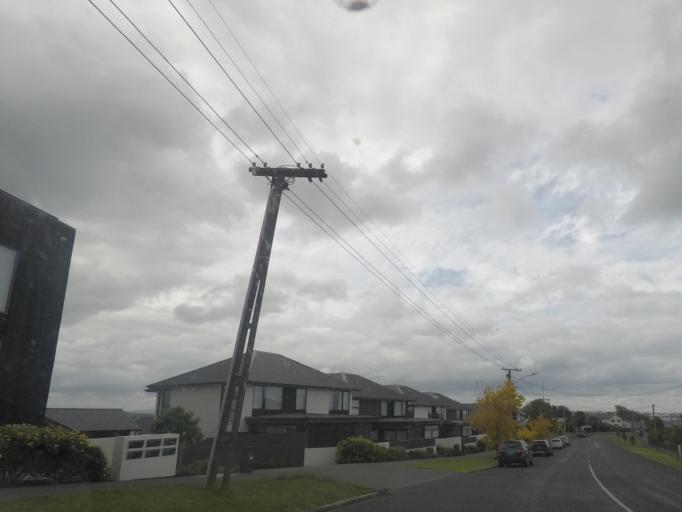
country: NZ
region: Auckland
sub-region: Auckland
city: Tamaki
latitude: -36.8705
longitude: 174.8747
